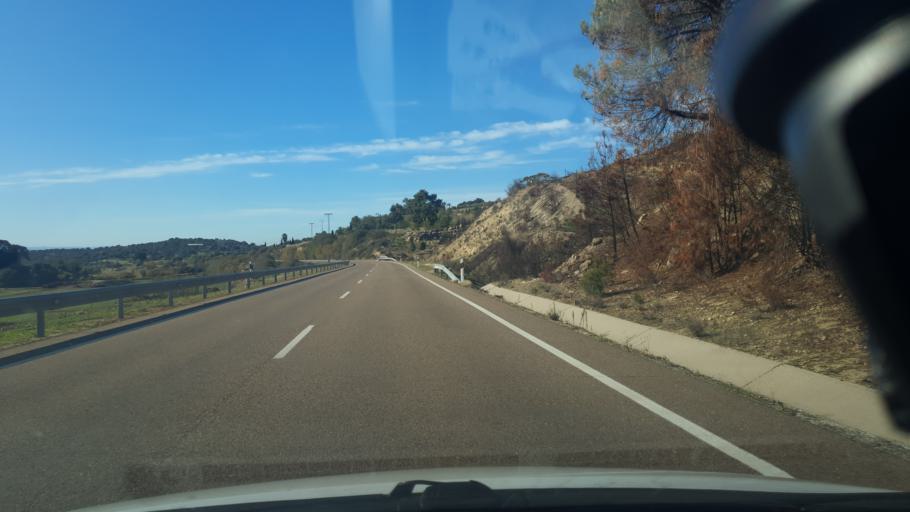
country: ES
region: Castille and Leon
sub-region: Provincia de Avila
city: Poyales del Hoyo
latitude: 40.1641
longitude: -5.1411
